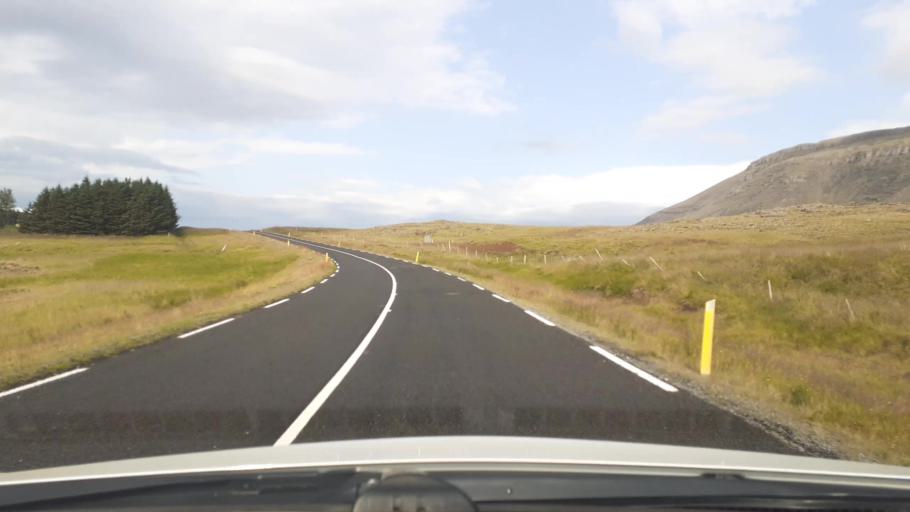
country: IS
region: Capital Region
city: Mosfellsbaer
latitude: 64.3424
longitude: -21.5852
